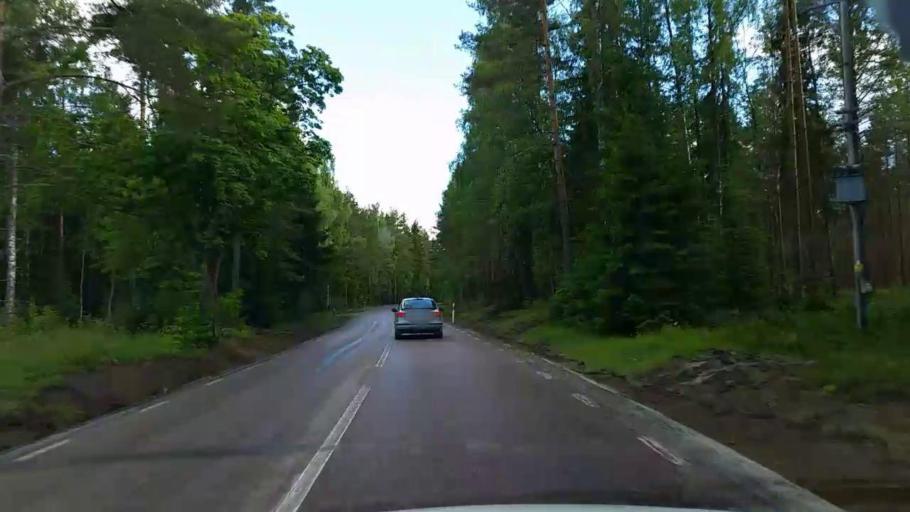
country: SE
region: Vaestmanland
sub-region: Fagersta Kommun
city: Fagersta
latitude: 59.9108
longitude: 15.8238
